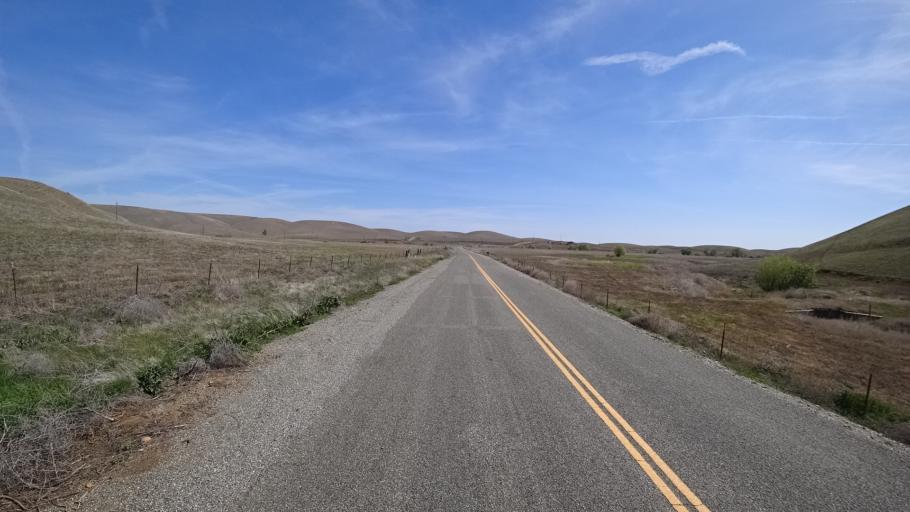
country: US
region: California
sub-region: Glenn County
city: Willows
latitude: 39.5509
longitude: -122.3637
